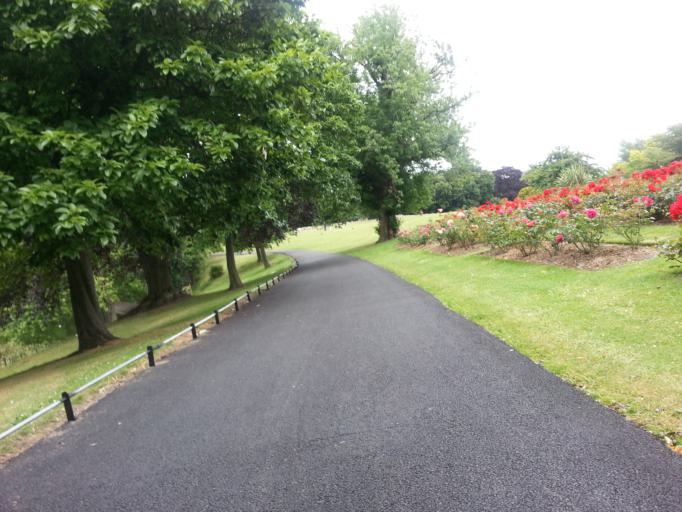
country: IE
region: Leinster
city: Rialto
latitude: 53.3511
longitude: -6.3014
